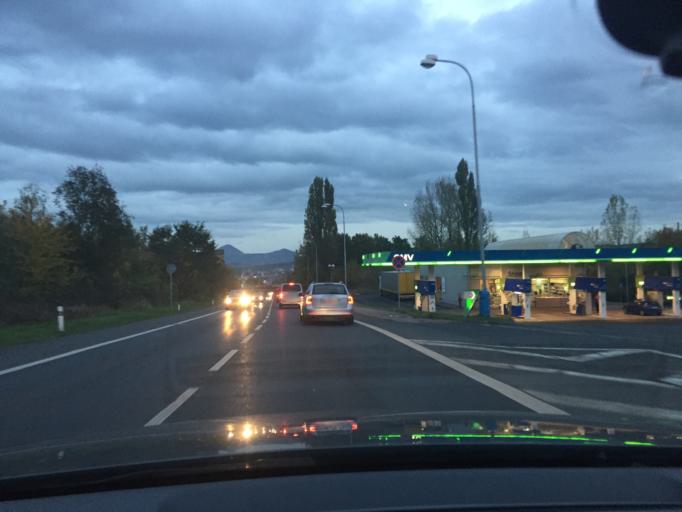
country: CZ
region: Ustecky
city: Novosedlice
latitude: 50.6553
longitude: 13.8067
